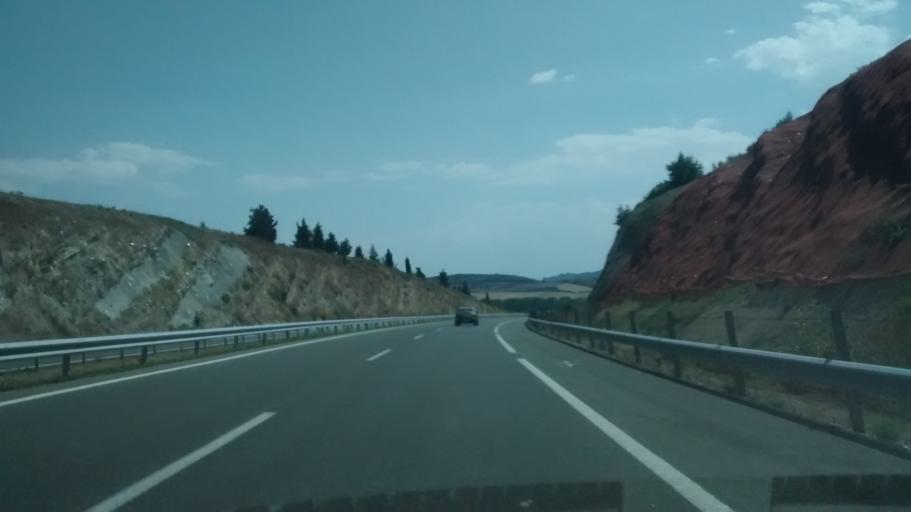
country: ES
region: Basque Country
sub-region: Provincia de Alava
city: Arminon
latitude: 42.6955
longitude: -2.8927
